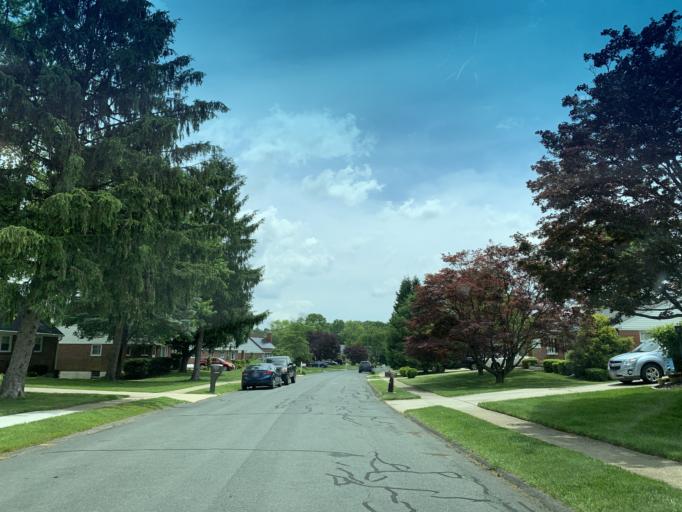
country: US
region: Maryland
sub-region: Harford County
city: South Bel Air
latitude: 39.5381
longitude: -76.2998
